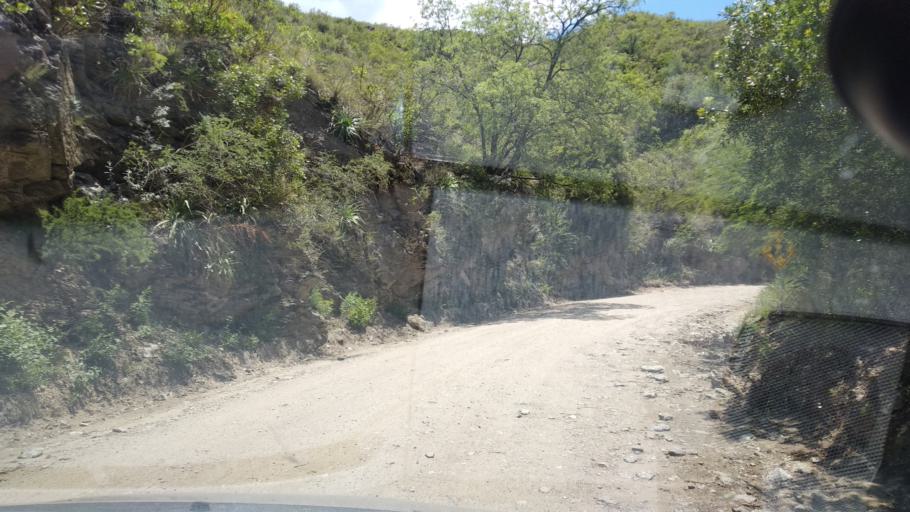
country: AR
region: Cordoba
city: Salsacate
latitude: -31.3766
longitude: -65.4039
